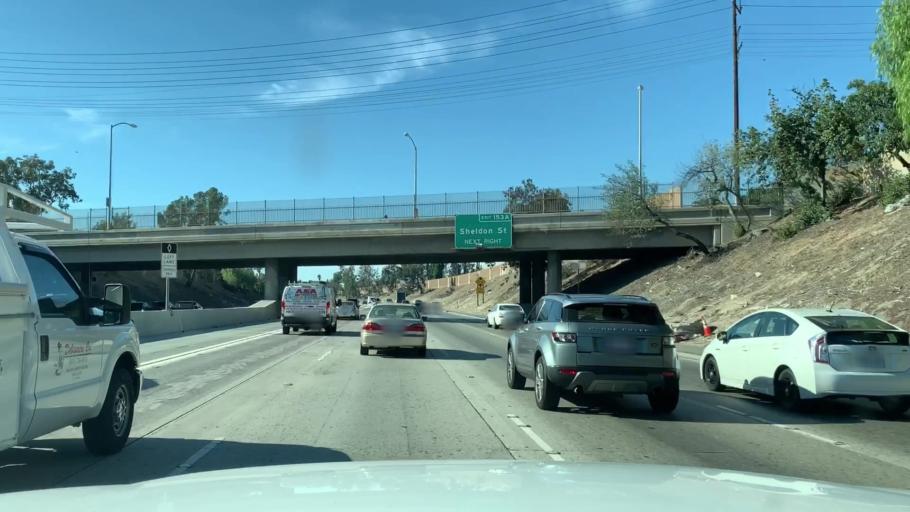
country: US
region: California
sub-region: Los Angeles County
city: North Hollywood
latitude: 34.2287
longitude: -118.3925
